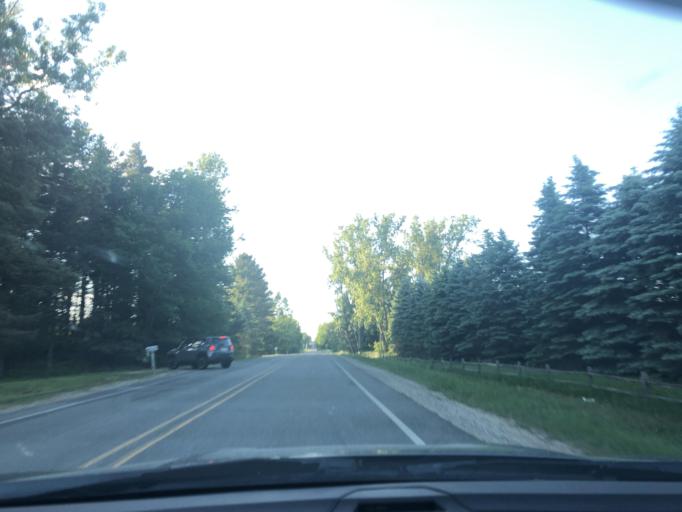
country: US
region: Michigan
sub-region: Missaukee County
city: Lake City
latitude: 44.4499
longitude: -85.0747
